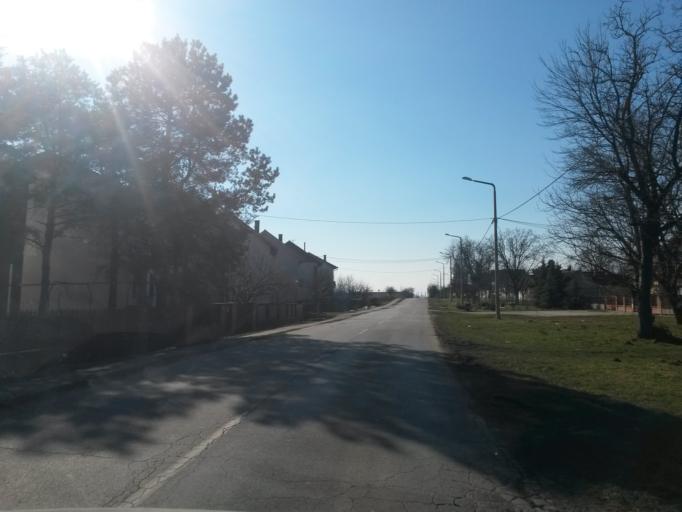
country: HR
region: Vukovarsko-Srijemska
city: Vukovar
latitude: 45.3314
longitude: 18.9959
